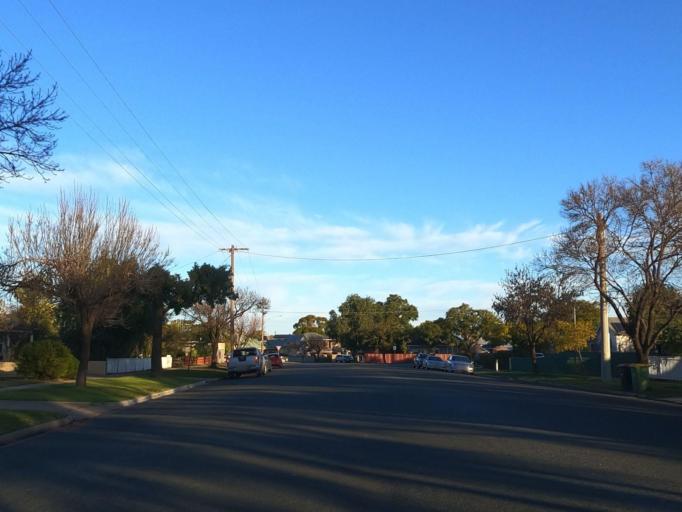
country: AU
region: Victoria
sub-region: Swan Hill
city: Swan Hill
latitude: -35.3473
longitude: 143.5604
